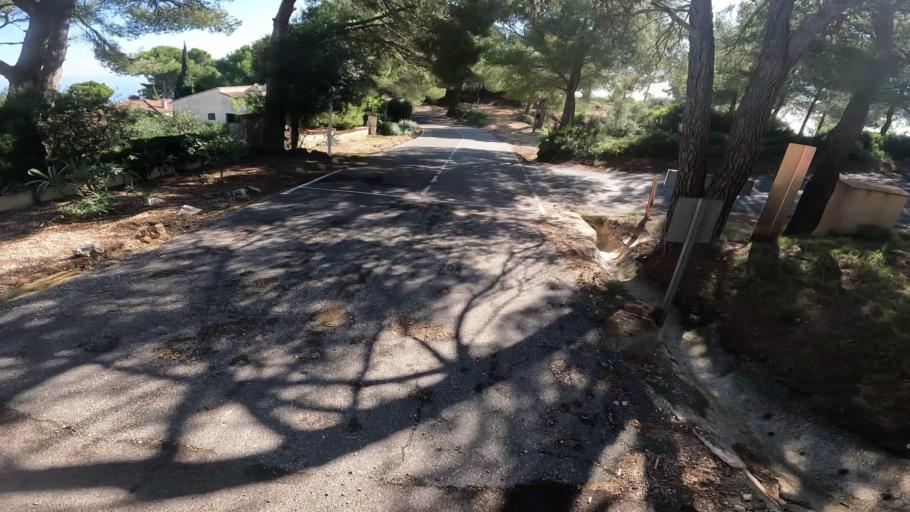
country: ES
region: Valencia
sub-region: Provincia de Castello
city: Alcoceber
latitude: 40.2650
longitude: 0.2730
